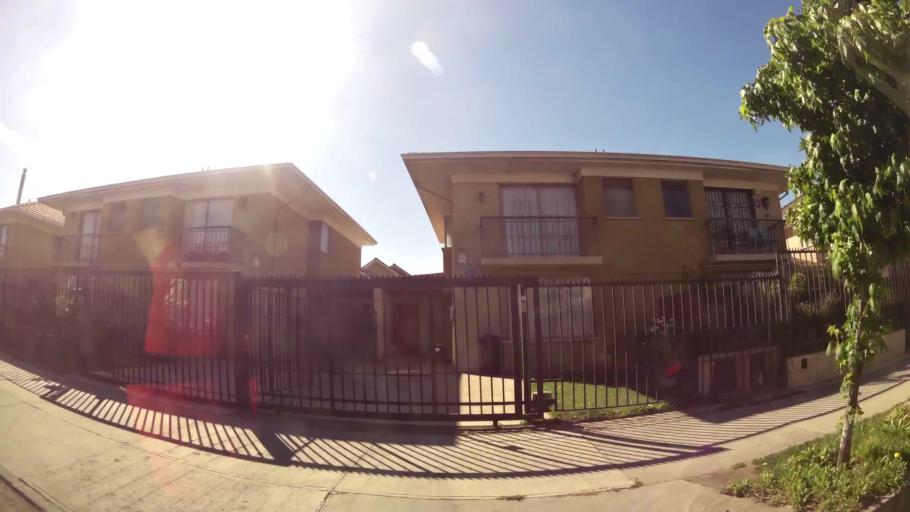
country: CL
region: Santiago Metropolitan
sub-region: Provincia de Maipo
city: San Bernardo
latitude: -33.5594
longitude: -70.7800
